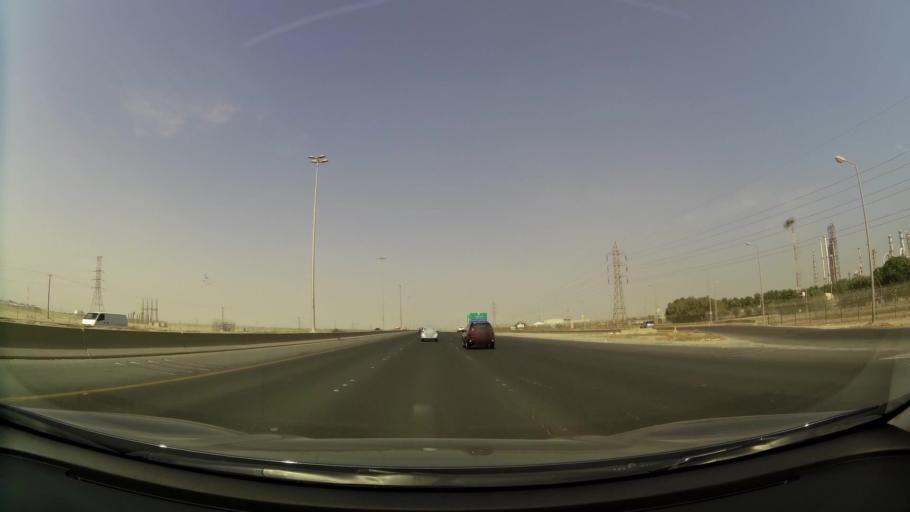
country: KW
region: Al Ahmadi
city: Al Fahahil
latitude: 29.0226
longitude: 48.1263
